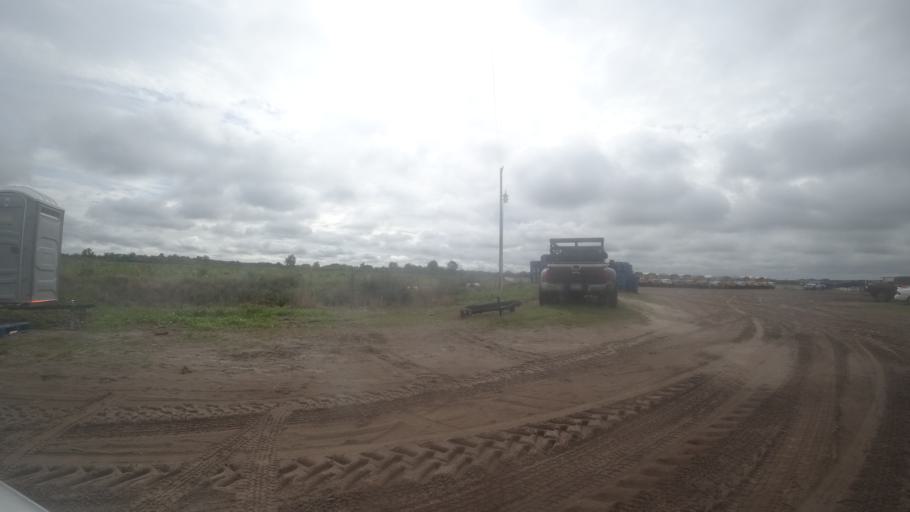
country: US
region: Florida
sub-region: Sarasota County
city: Warm Mineral Springs
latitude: 27.2802
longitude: -82.1699
